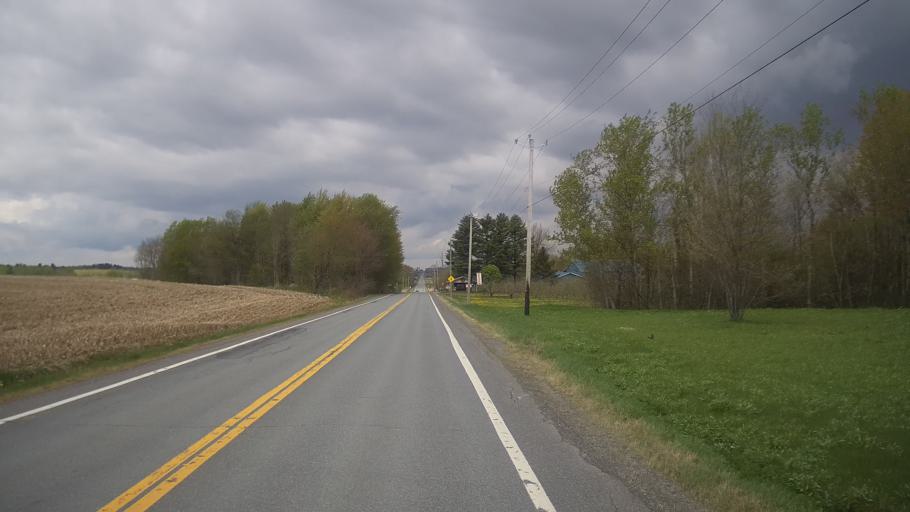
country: CA
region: Quebec
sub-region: Monteregie
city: Farnham
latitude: 45.2471
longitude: -72.8923
